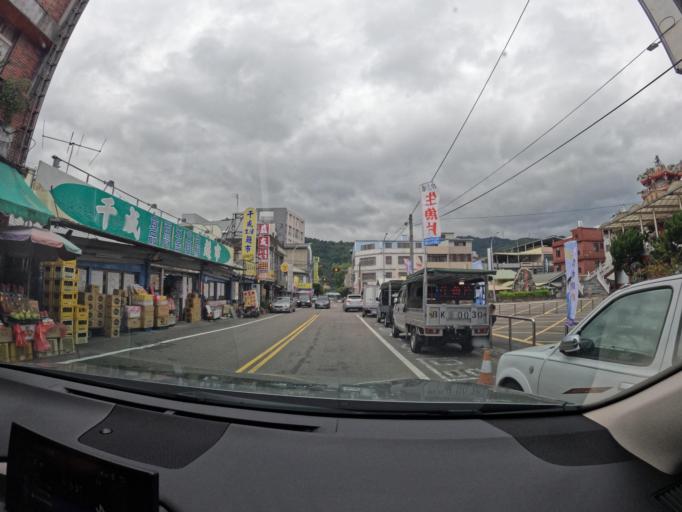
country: TW
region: Taiwan
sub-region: Miaoli
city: Miaoli
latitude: 24.4240
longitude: 120.8678
